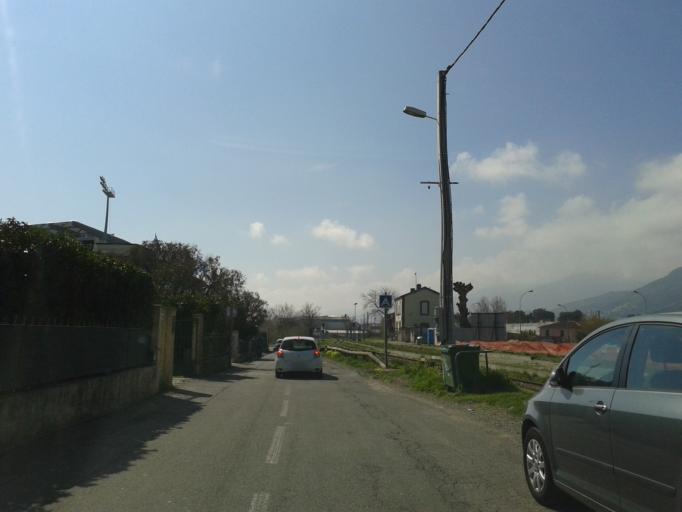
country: FR
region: Corsica
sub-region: Departement de la Haute-Corse
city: Furiani
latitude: 42.6526
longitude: 9.4415
